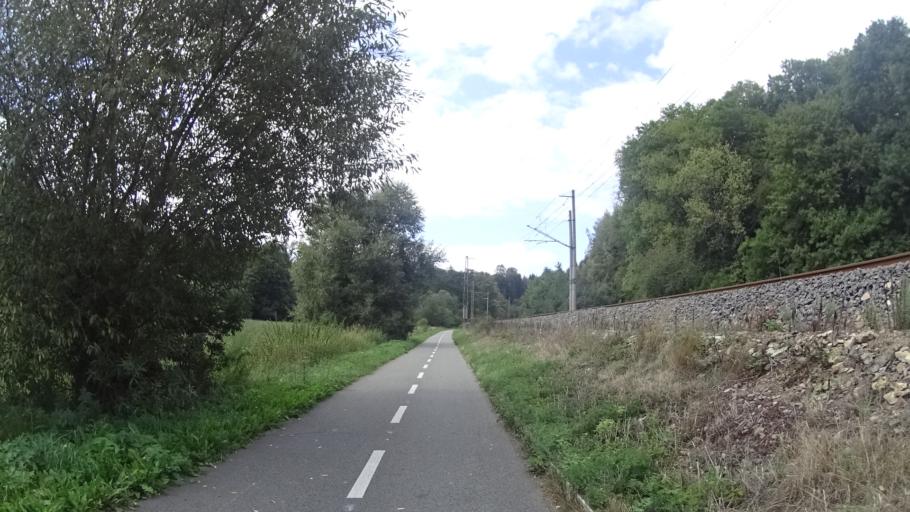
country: CZ
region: Pardubicky
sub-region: Okres Usti nad Orlici
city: Usti nad Orlici
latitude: 49.9863
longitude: 16.4159
